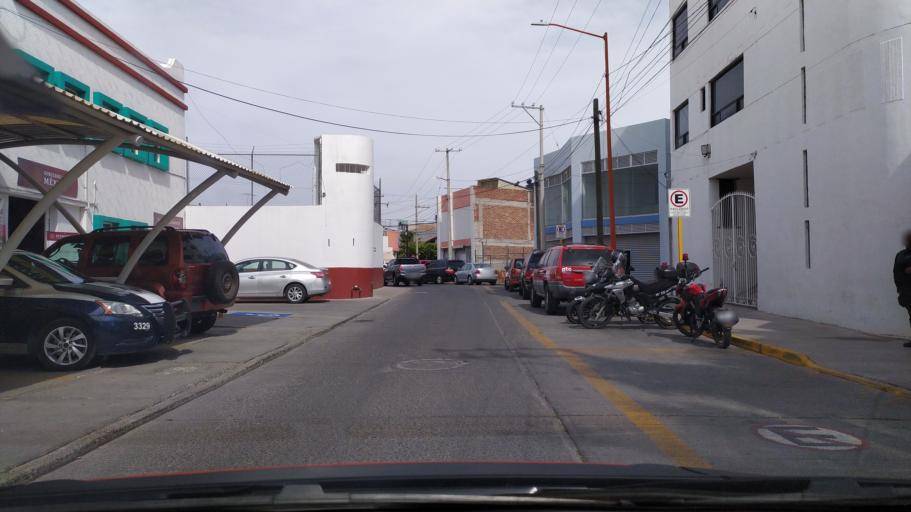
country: MX
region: Guanajuato
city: San Francisco del Rincon
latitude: 21.0164
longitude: -101.8617
